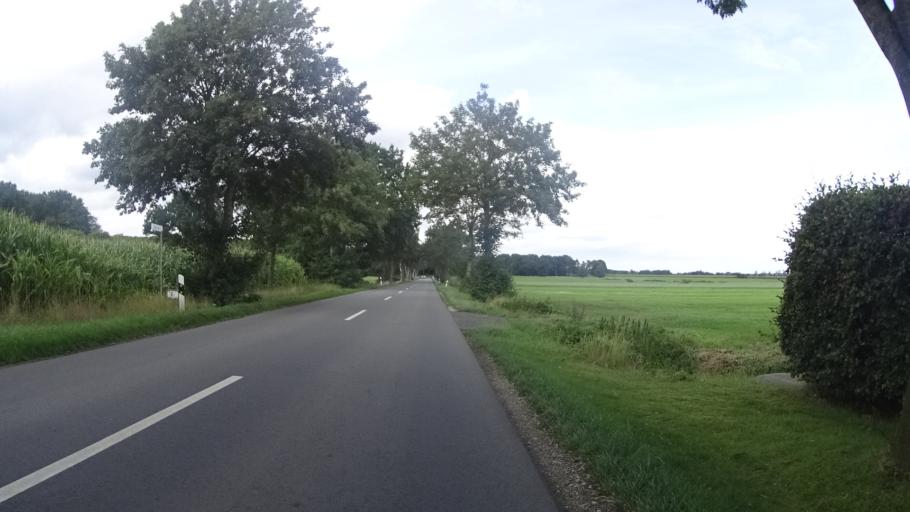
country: DE
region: Lower Saxony
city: Mittelstenahe
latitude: 53.6551
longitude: 9.0354
